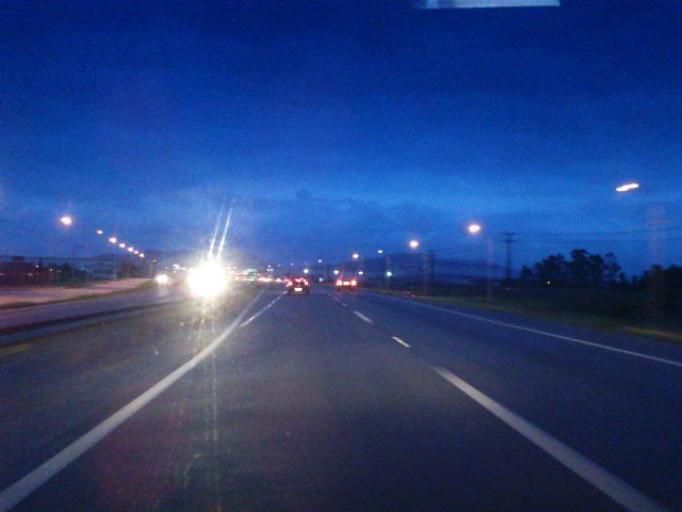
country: BR
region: Santa Catarina
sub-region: Itajai
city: Itajai
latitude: -26.8518
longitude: -48.7264
